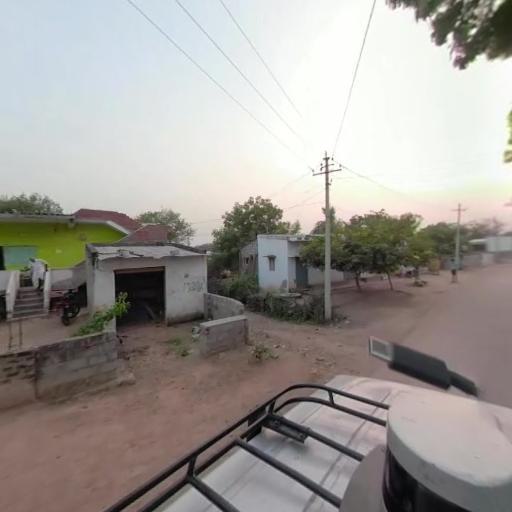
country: IN
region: Telangana
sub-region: Nalgonda
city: Suriapet
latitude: 17.1055
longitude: 79.5284
